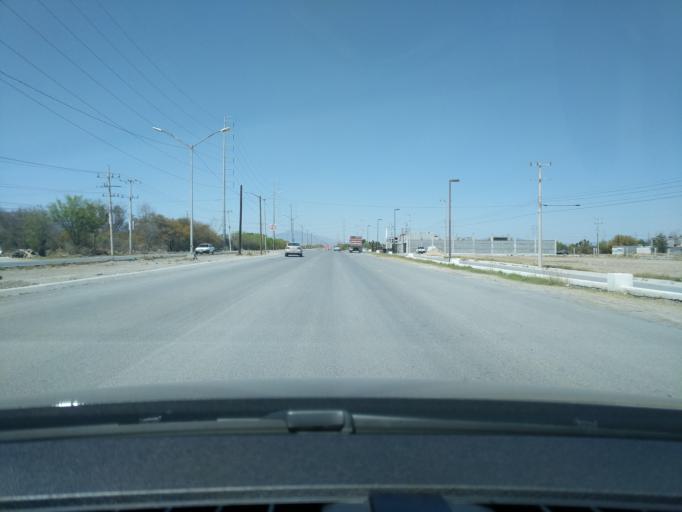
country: MX
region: Nuevo Leon
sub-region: Salinas Victoria
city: Emiliano Zapata
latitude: 25.9157
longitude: -100.2688
